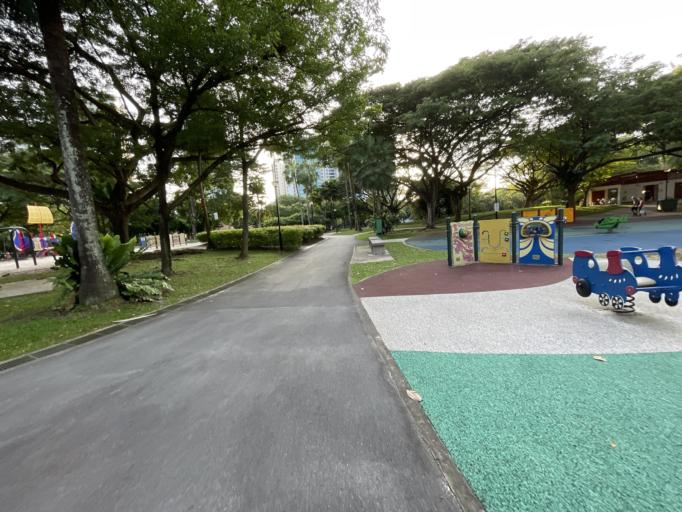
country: SG
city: Singapore
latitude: 1.2971
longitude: 103.7624
